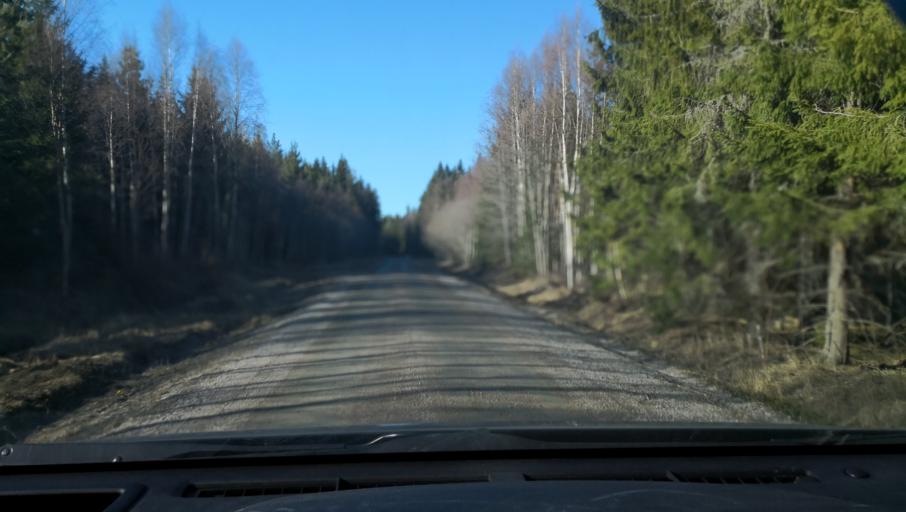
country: SE
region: Vaestmanland
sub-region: Sala Kommun
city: Sala
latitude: 60.1398
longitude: 16.6490
